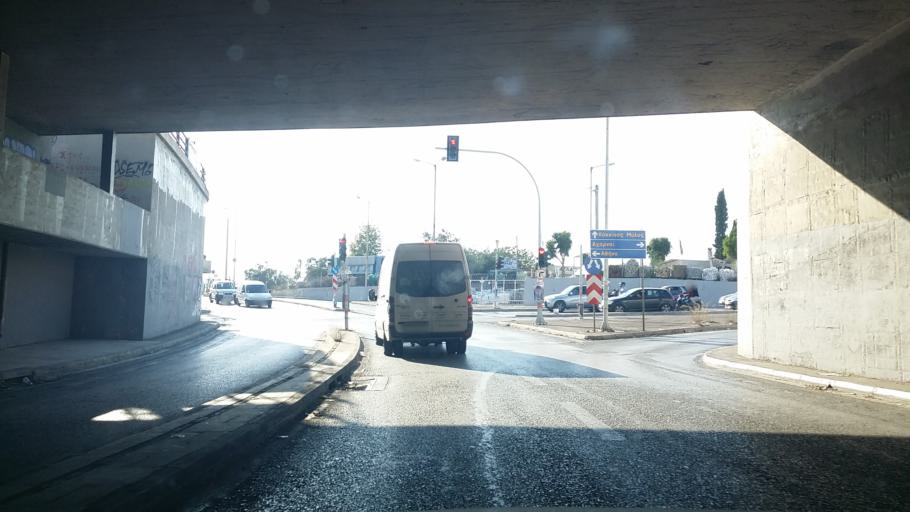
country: GR
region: Attica
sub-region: Nomarchia Athinas
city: Irakleio
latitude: 38.0551
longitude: 23.7458
